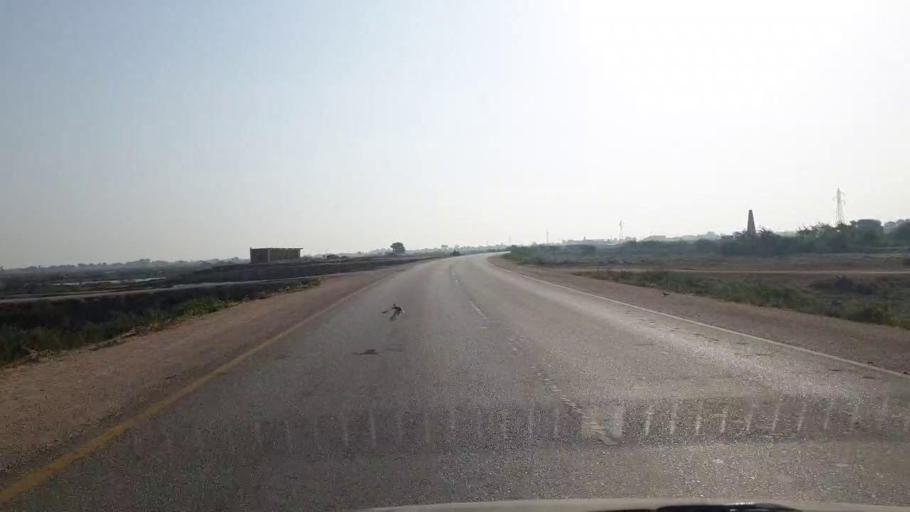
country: PK
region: Sindh
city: Badin
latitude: 24.6809
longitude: 68.8386
